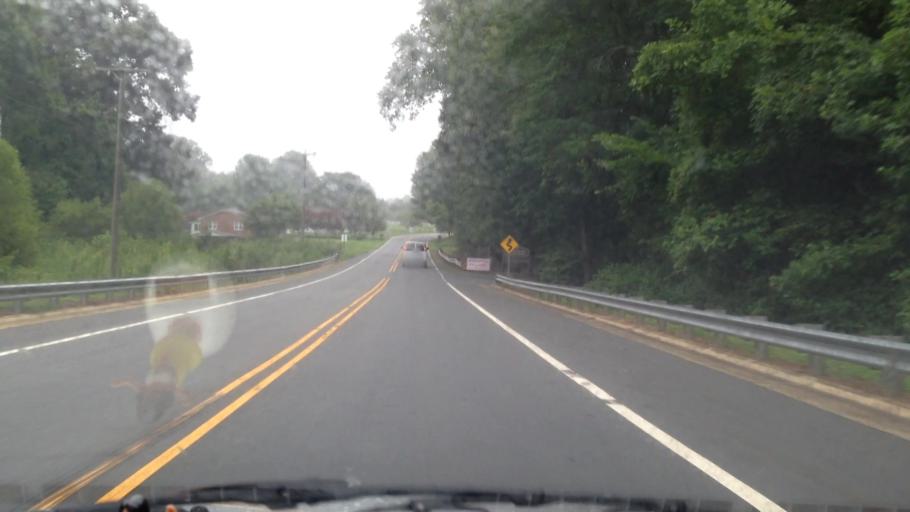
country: US
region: North Carolina
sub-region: Forsyth County
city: Kernersville
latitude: 36.1559
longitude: -80.1001
